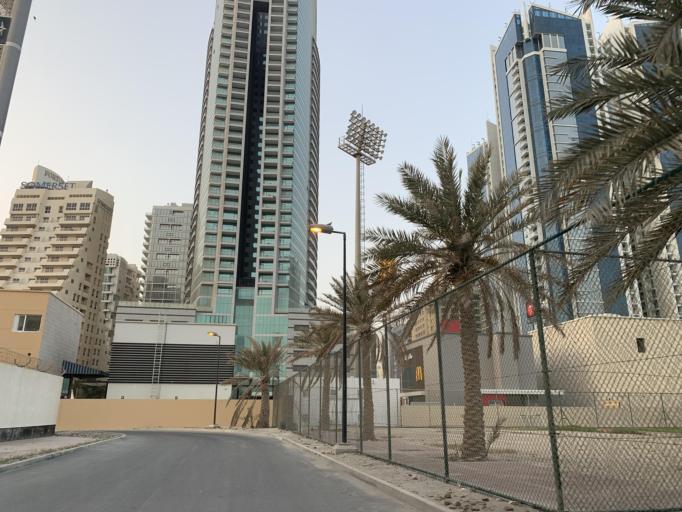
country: BH
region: Manama
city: Manama
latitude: 26.2252
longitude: 50.6092
